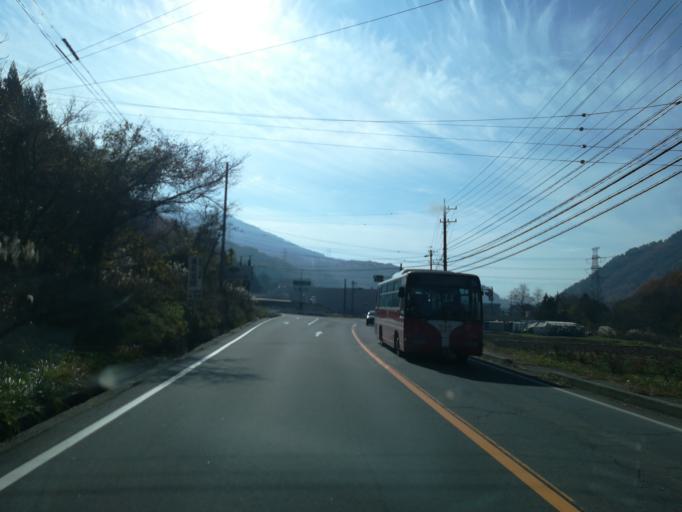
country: JP
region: Nagano
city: Ueda
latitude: 36.4612
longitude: 138.3397
